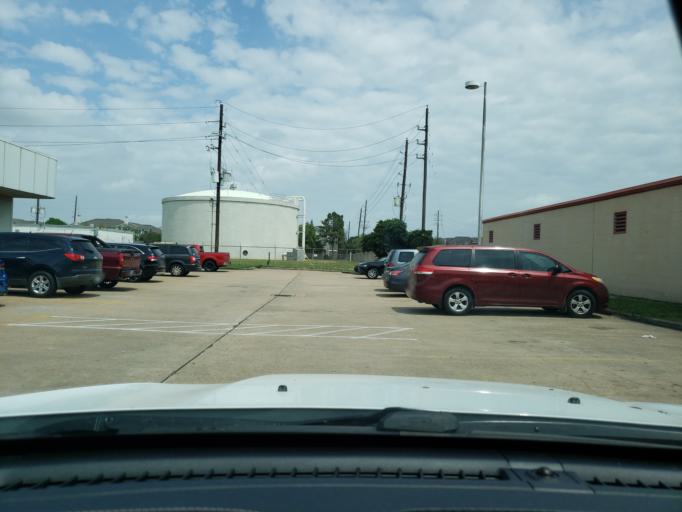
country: US
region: Texas
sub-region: Fort Bend County
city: Cinco Ranch
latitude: 29.7901
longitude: -95.7272
